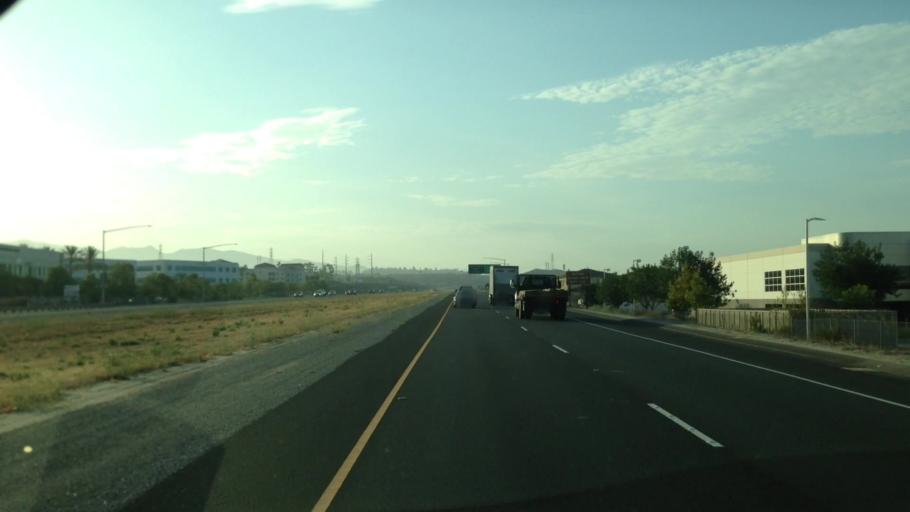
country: US
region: California
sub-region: Orange County
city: Foothill Ranch
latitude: 33.6708
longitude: -117.6583
